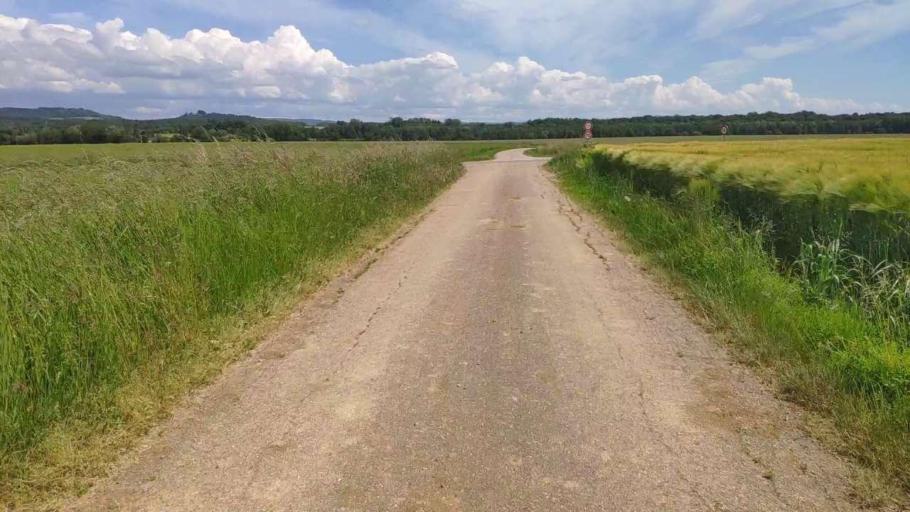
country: FR
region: Franche-Comte
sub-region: Departement du Jura
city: Bletterans
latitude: 46.7345
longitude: 5.4824
